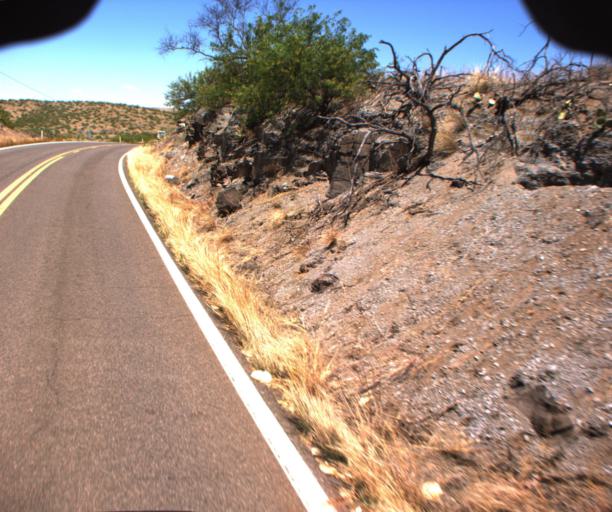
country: US
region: Arizona
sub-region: Cochise County
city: Douglas
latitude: 31.4651
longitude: -109.3828
